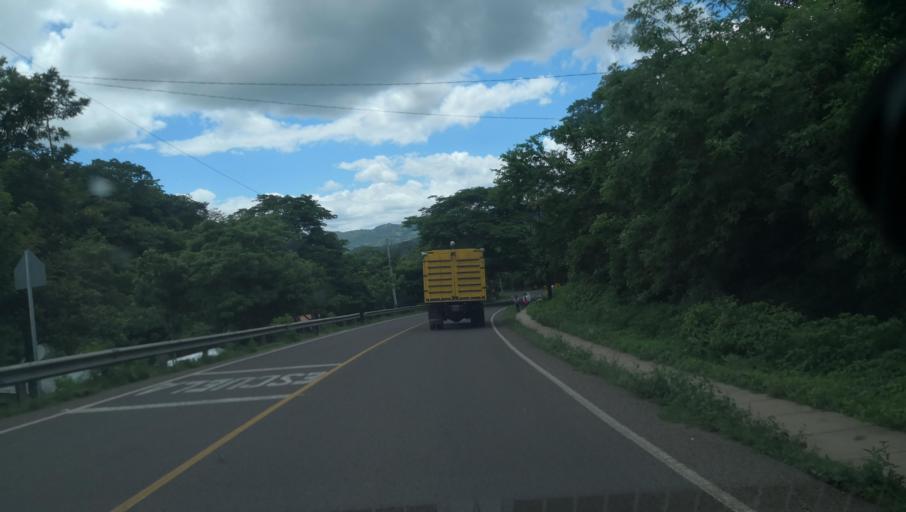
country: NI
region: Madriz
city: Yalaguina
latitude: 13.4646
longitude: -86.4698
